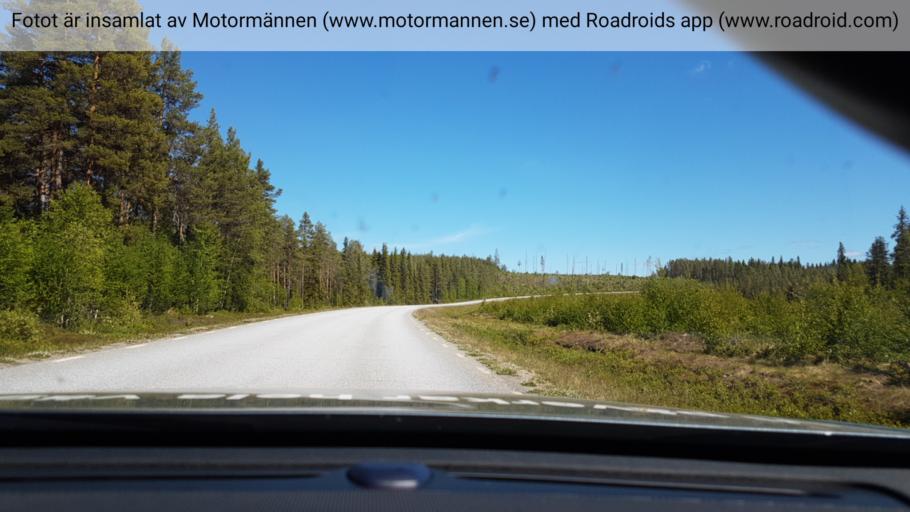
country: SE
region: Vaesterbotten
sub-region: Vilhelmina Kommun
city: Vilhelmina
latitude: 64.6331
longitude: 16.9080
